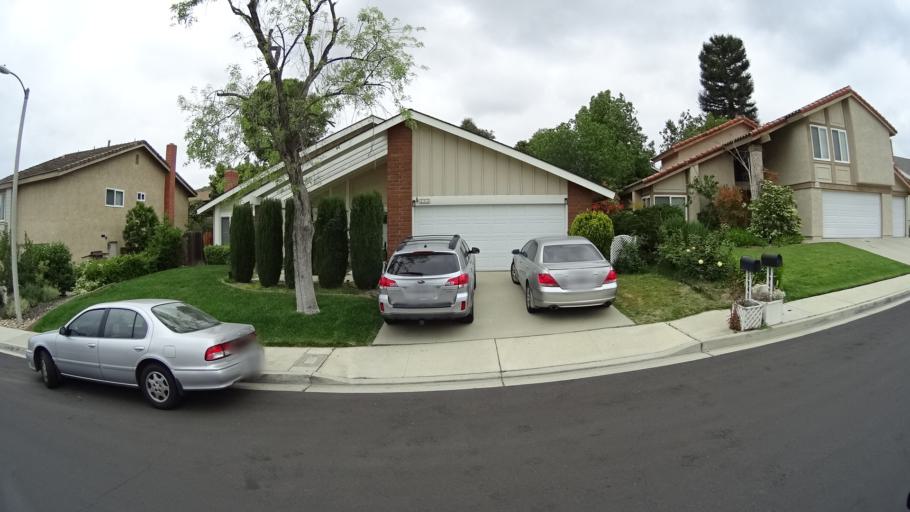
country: US
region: California
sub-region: Ventura County
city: Thousand Oaks
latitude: 34.2189
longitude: -118.8826
